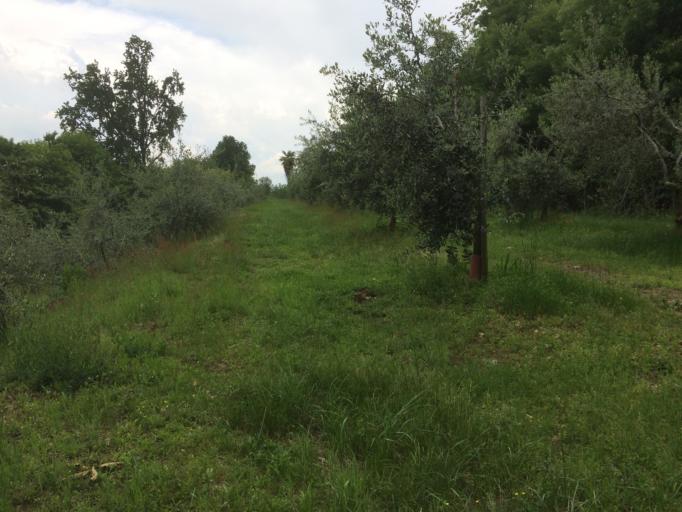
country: IT
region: Piedmont
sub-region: Provincia di Torino
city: Vialfre
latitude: 45.3797
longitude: 7.8241
